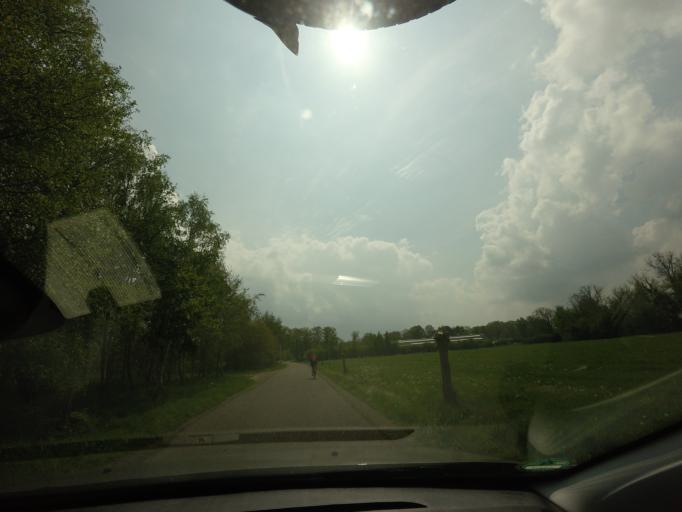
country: NL
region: Overijssel
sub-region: Gemeente Haaksbergen
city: Haaksbergen
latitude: 52.1793
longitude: 6.8086
